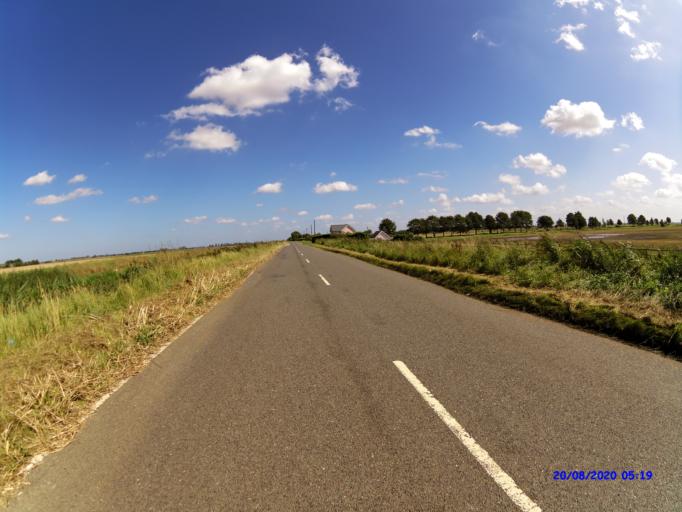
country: GB
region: England
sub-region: Cambridgeshire
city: Whittlesey
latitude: 52.5271
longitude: -0.1062
